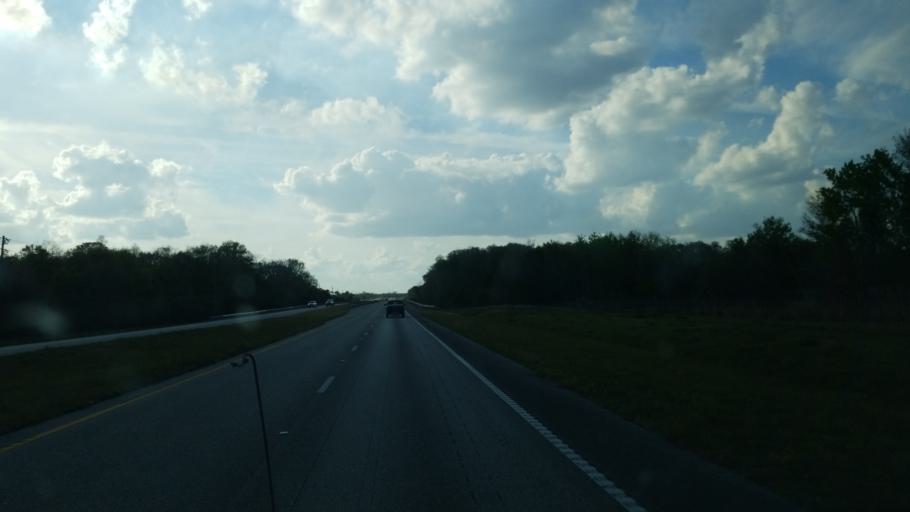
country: US
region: Florida
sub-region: Osceola County
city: Saint Cloud
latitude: 28.1301
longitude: -80.9987
